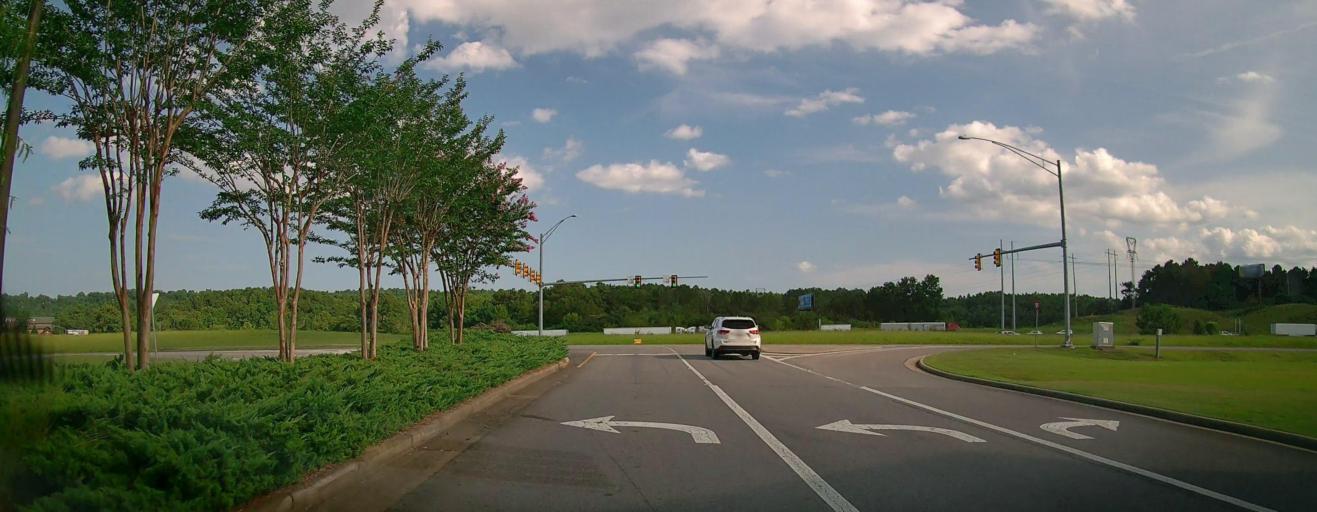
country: US
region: Alabama
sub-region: Jefferson County
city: Leeds
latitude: 33.5319
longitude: -86.5966
